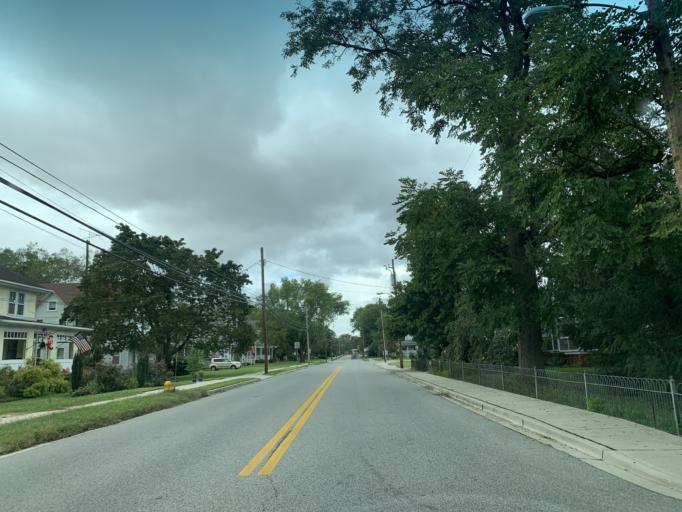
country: US
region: Maryland
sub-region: Caroline County
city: Denton
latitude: 38.8807
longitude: -75.8286
